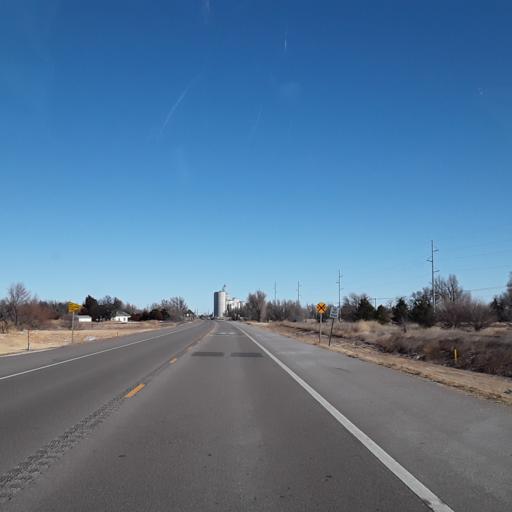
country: US
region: Kansas
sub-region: Pawnee County
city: Larned
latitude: 38.1683
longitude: -99.1094
